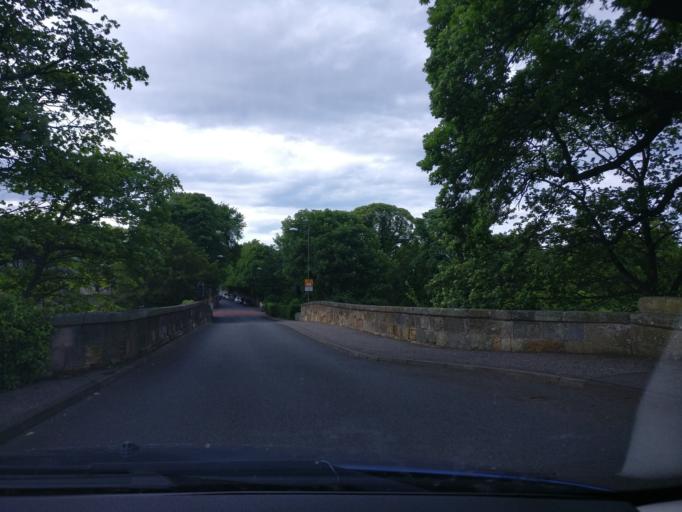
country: GB
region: Scotland
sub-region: East Lothian
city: Haddington
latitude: 55.9507
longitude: -2.7735
